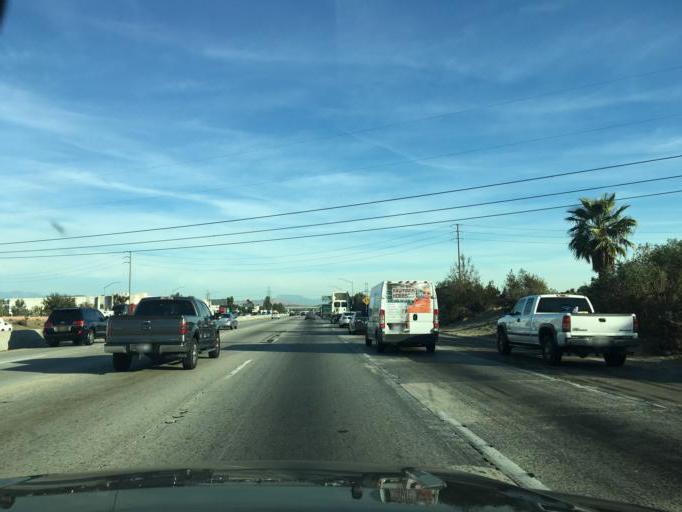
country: US
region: California
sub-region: Riverside County
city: Mira Loma
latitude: 34.0284
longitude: -117.5742
